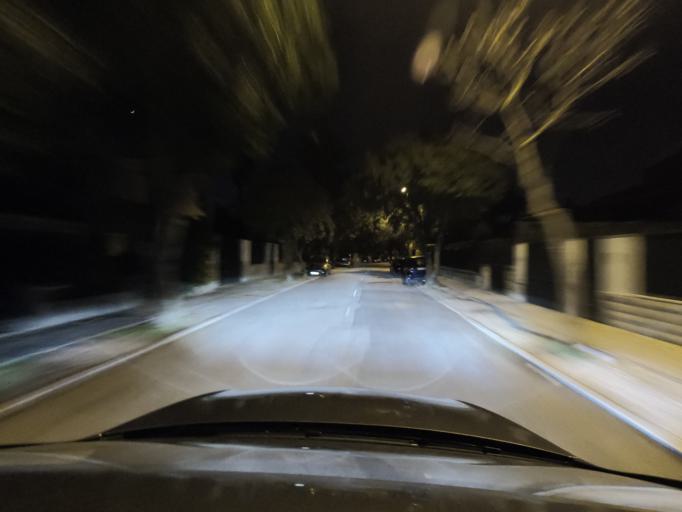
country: PT
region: Lisbon
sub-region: Oeiras
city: Carcavelos
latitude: 38.6897
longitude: -9.3237
